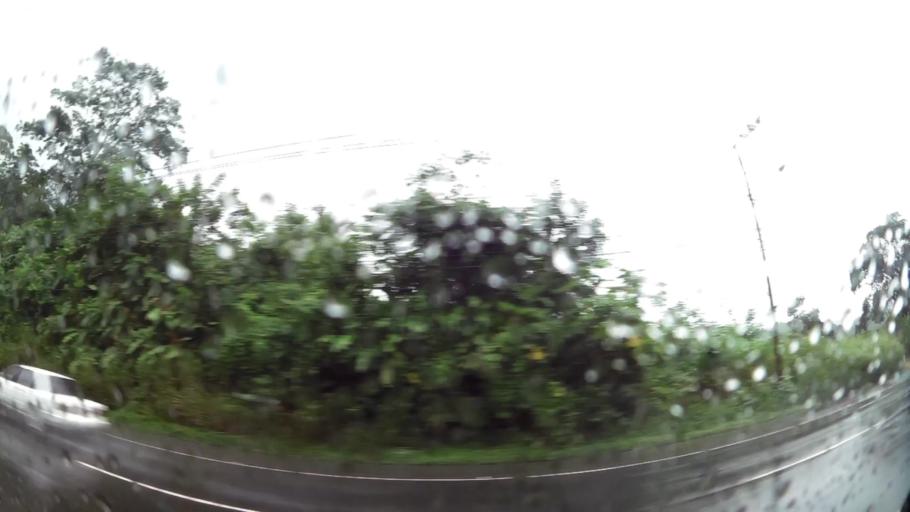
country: PA
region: Colon
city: Quebrada Bonita Adentro
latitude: 9.2829
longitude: -79.7101
